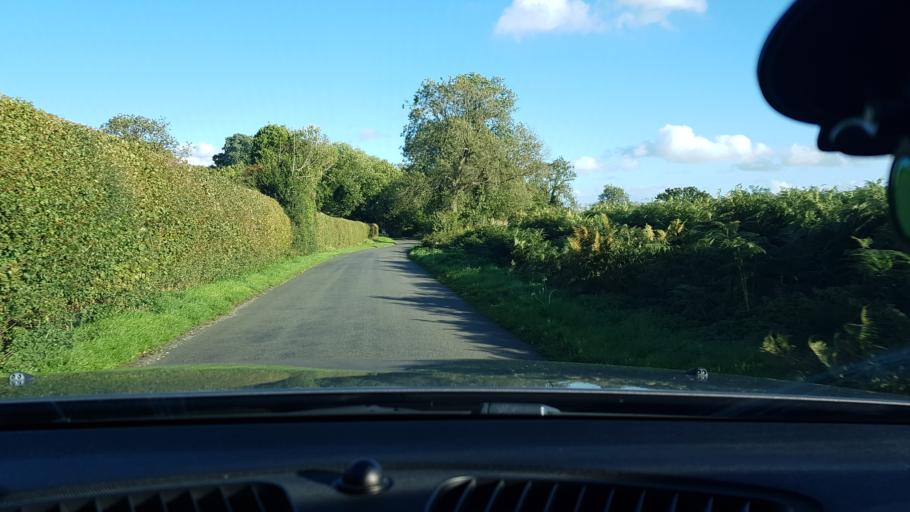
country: GB
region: England
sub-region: Wiltshire
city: Chilton Foliat
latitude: 51.4662
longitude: -1.5524
